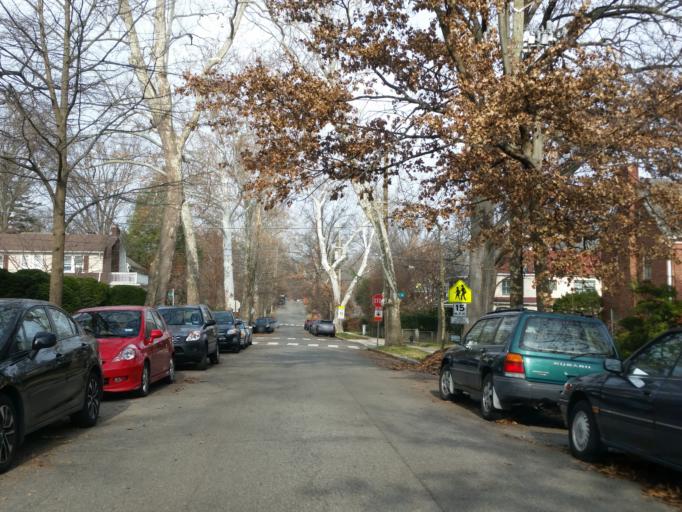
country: US
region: Maryland
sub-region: Montgomery County
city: Chevy Chase
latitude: 38.9654
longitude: -77.0664
